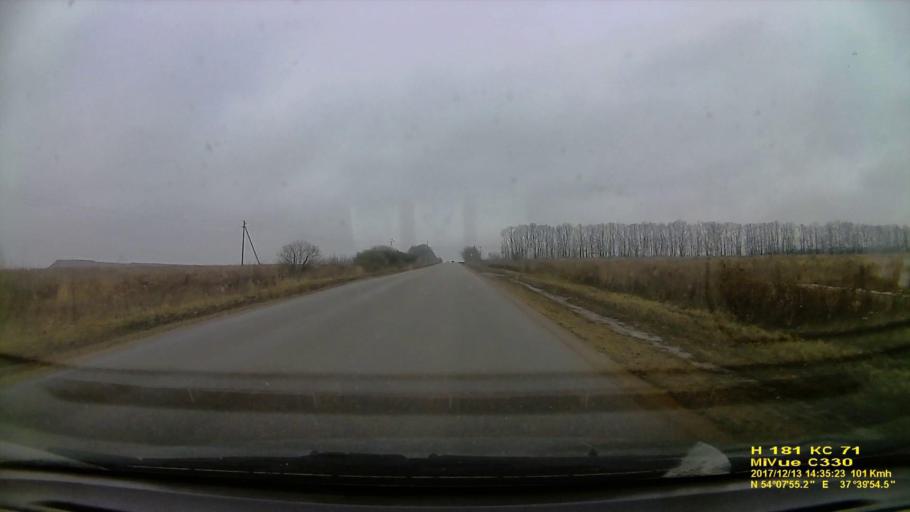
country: RU
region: Tula
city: Skuratovskiy
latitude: 54.1322
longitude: 37.6651
